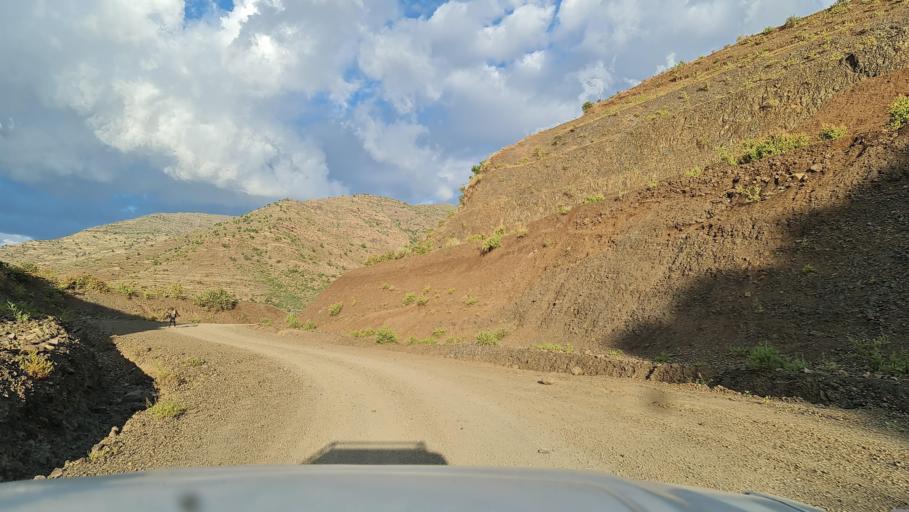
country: ET
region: Amhara
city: Debark'
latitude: 13.0266
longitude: 38.0529
